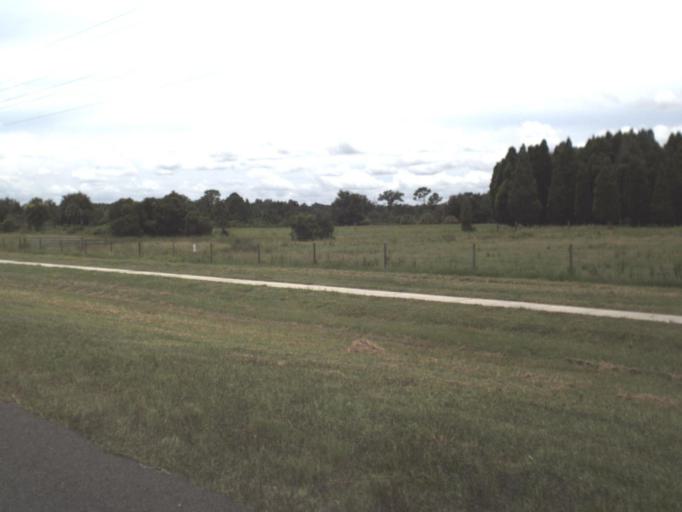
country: US
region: Florida
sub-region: Pasco County
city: Wesley Chapel
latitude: 28.1958
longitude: -82.3332
